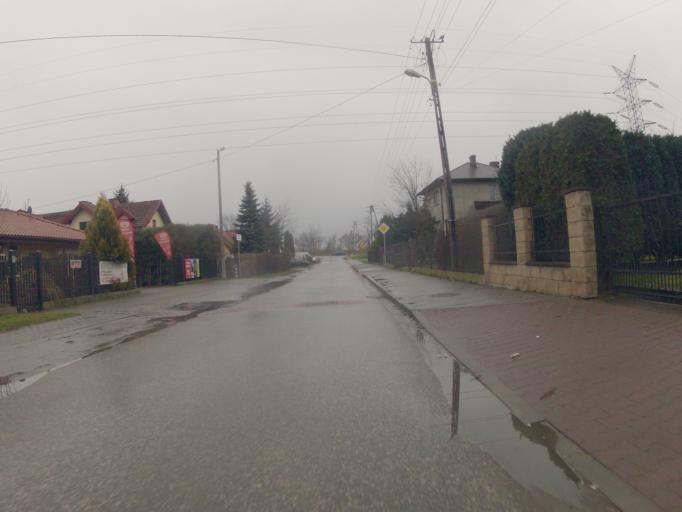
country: PL
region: Lesser Poland Voivodeship
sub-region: Powiat wielicki
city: Kokotow
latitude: 50.0549
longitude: 20.0456
